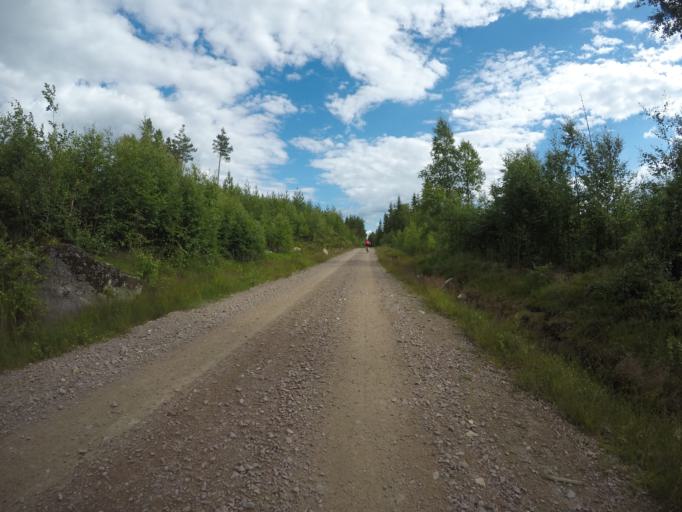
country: SE
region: Vaermland
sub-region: Filipstads Kommun
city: Lesjofors
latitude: 60.0729
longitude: 14.4295
